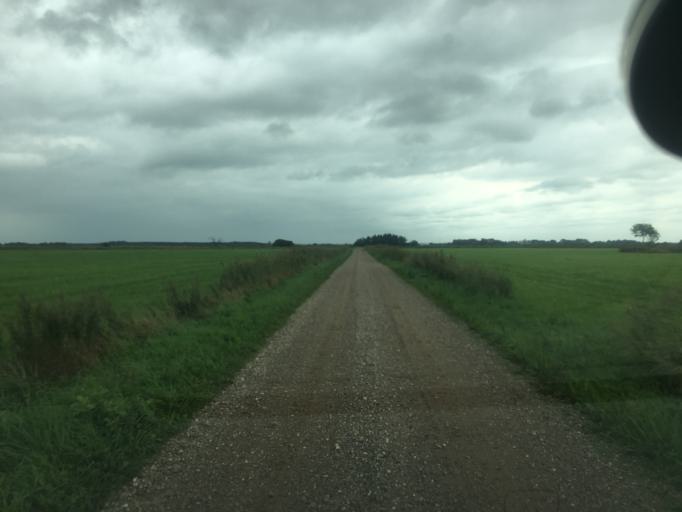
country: DK
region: South Denmark
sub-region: Tonder Kommune
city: Tonder
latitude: 54.9738
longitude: 8.9324
